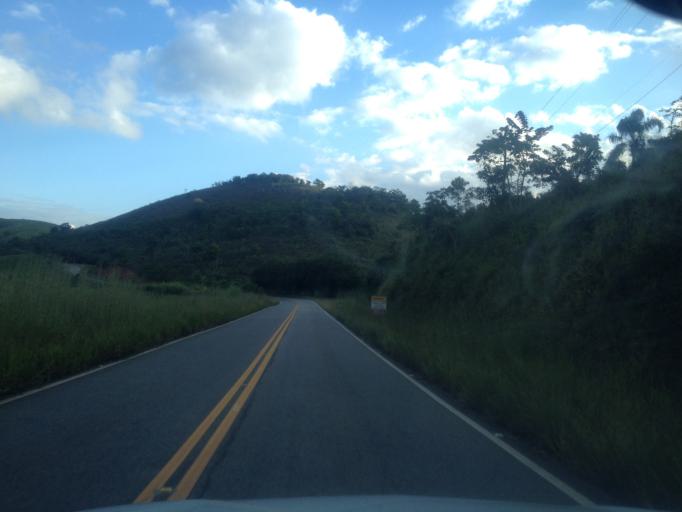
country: BR
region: Rio de Janeiro
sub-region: Quatis
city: Quatis
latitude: -22.3680
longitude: -44.2599
